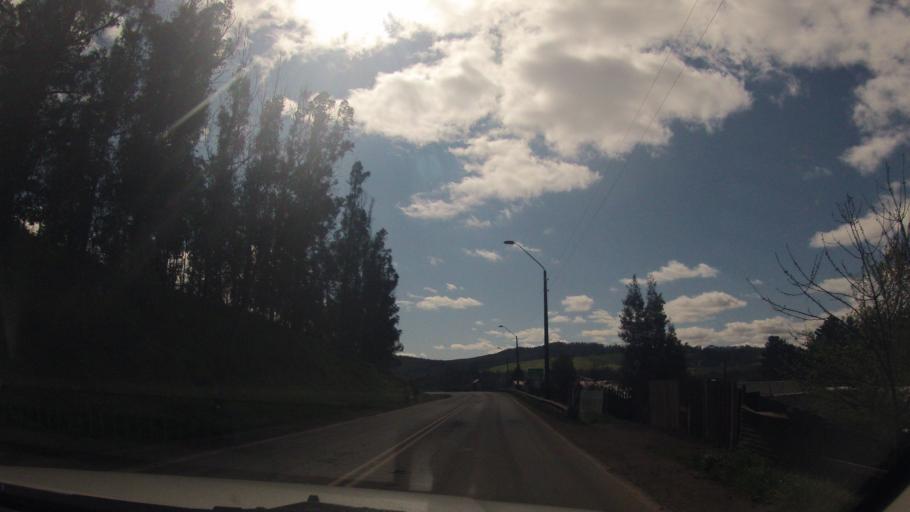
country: CL
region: Araucania
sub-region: Provincia de Malleco
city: Traiguen
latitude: -38.2481
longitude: -72.6817
